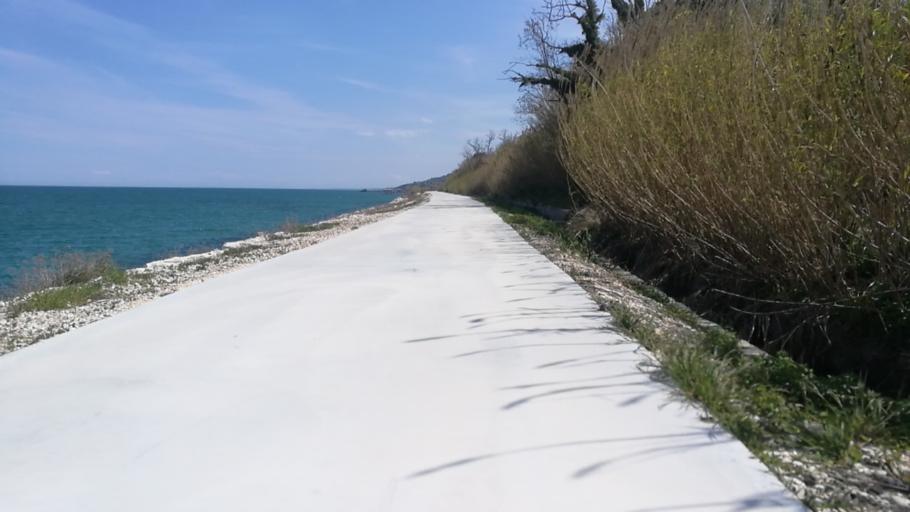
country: IT
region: Abruzzo
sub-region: Provincia di Chieti
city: Marina di San Vito
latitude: 42.3244
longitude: 14.4270
